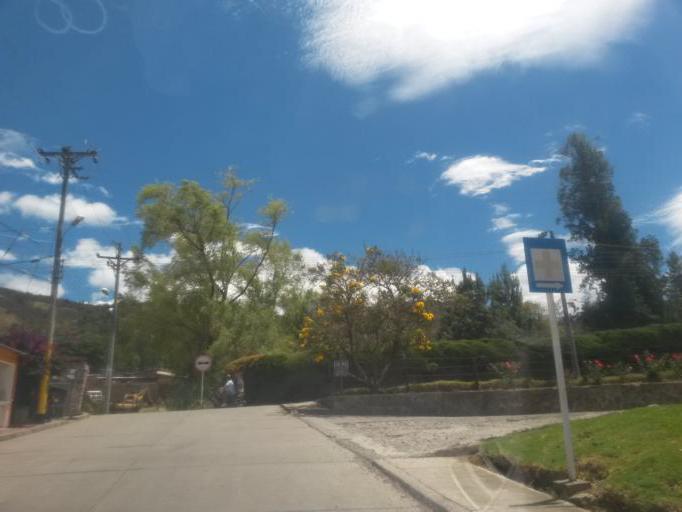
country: CO
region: Cauca
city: Silvia
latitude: 2.6109
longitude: -76.3831
